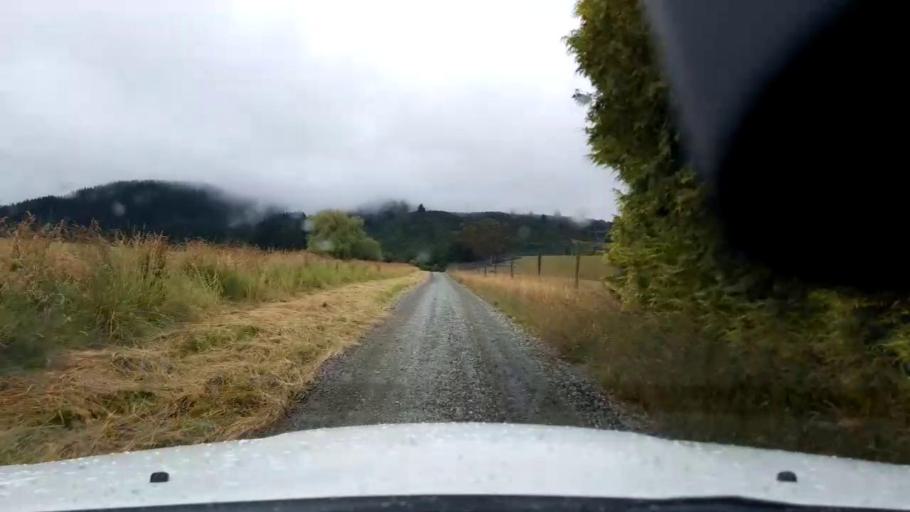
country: NZ
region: Canterbury
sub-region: Timaru District
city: Pleasant Point
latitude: -44.0760
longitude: 171.1444
